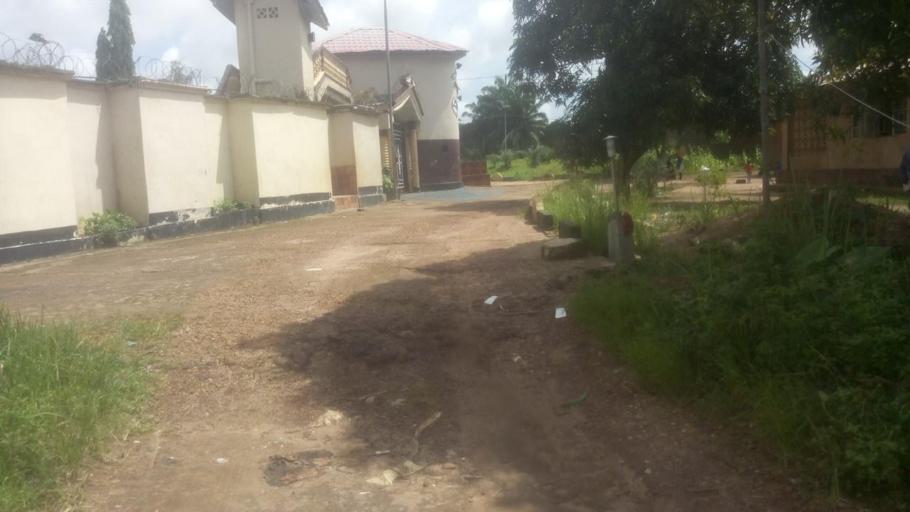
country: SL
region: Northern Province
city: Masoyila
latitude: 8.5946
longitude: -13.1873
